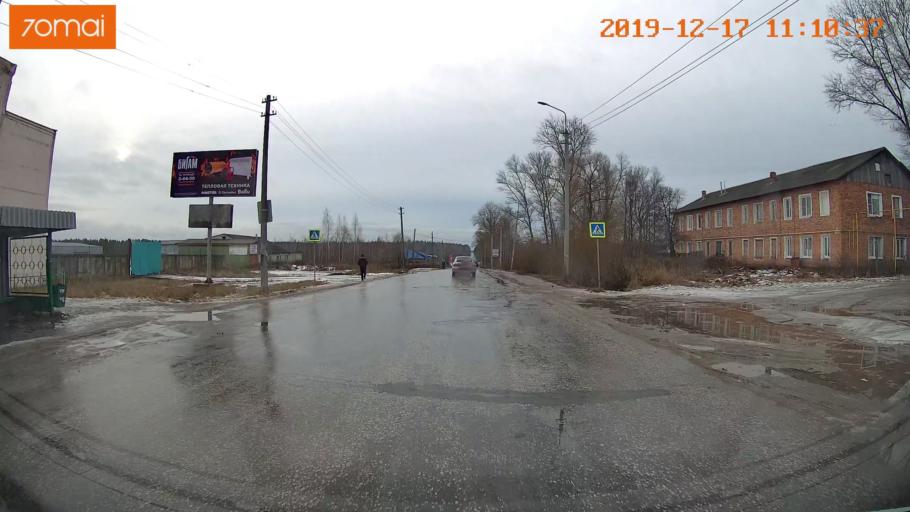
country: RU
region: Vladimir
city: Gus'-Khrustal'nyy
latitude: 55.5915
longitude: 40.6406
